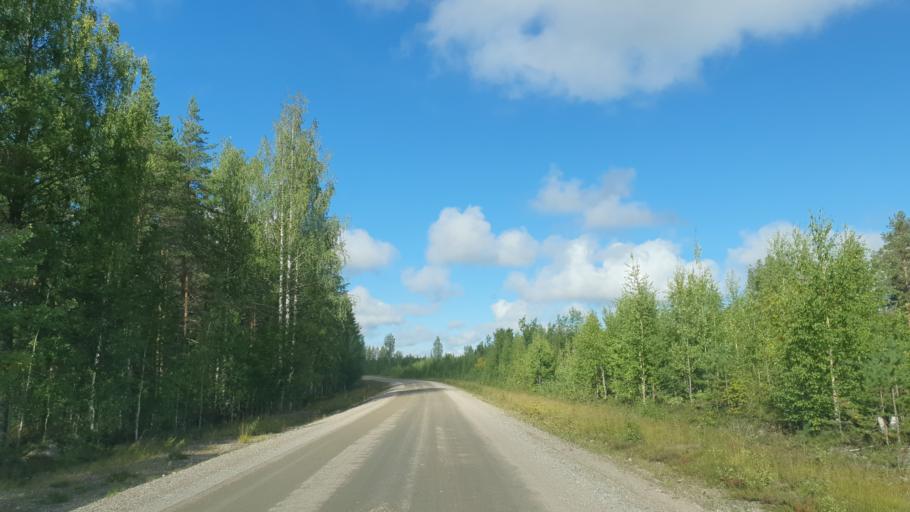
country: FI
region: Kainuu
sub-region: Kehys-Kainuu
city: Kuhmo
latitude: 63.9813
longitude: 29.2530
